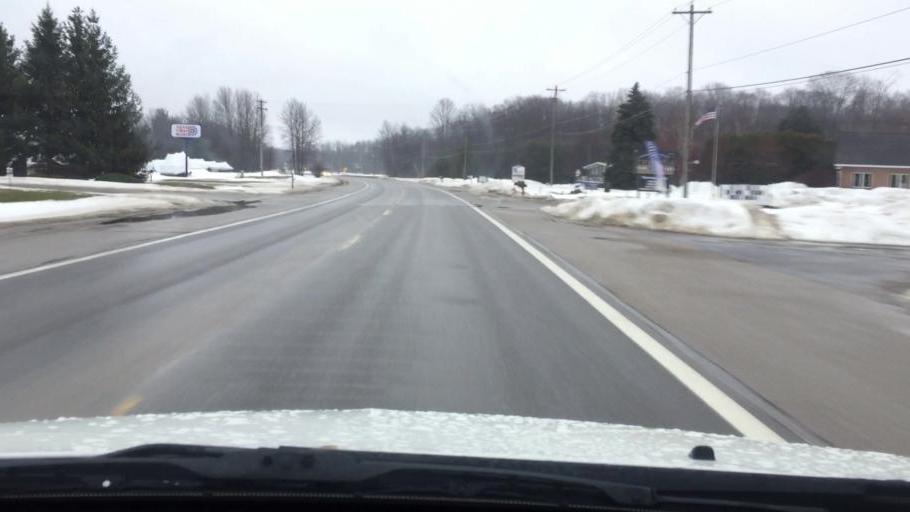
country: US
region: Michigan
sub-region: Charlevoix County
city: Charlevoix
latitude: 45.2980
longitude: -85.2555
